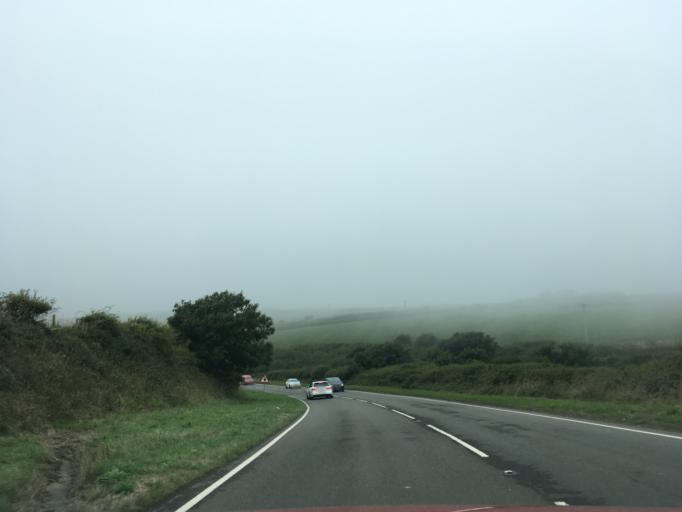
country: GB
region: Wales
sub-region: Pembrokeshire
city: Llanrhian
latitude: 51.8761
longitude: -5.1687
